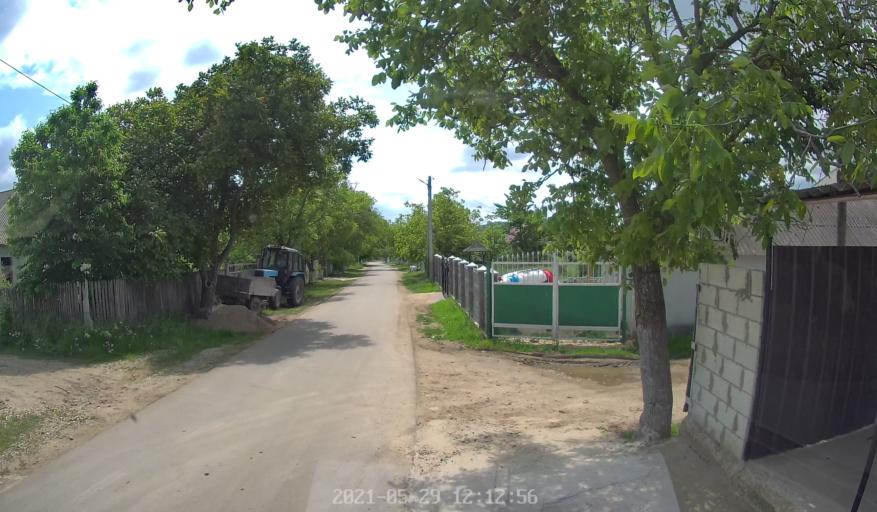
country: MD
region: Hincesti
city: Hincesti
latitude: 46.8774
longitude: 28.6323
